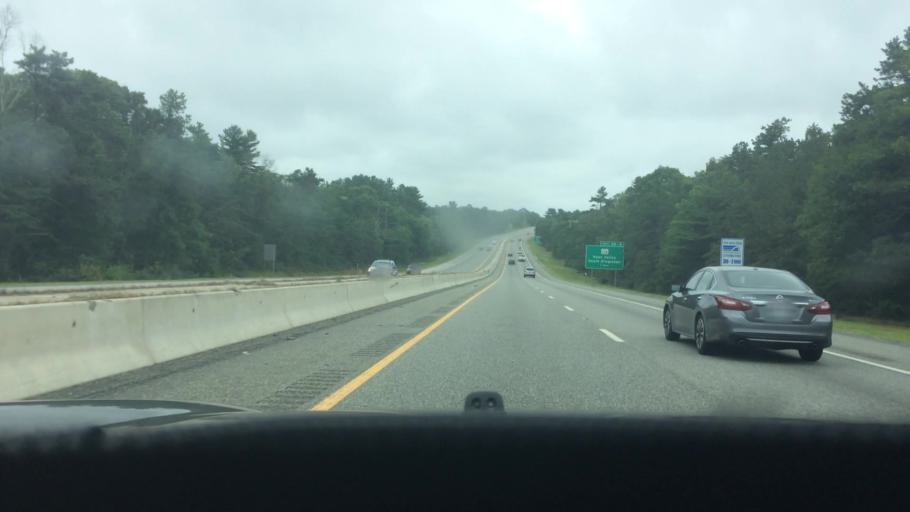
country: US
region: Rhode Island
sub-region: Washington County
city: Hope Valley
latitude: 41.5294
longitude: -71.6827
